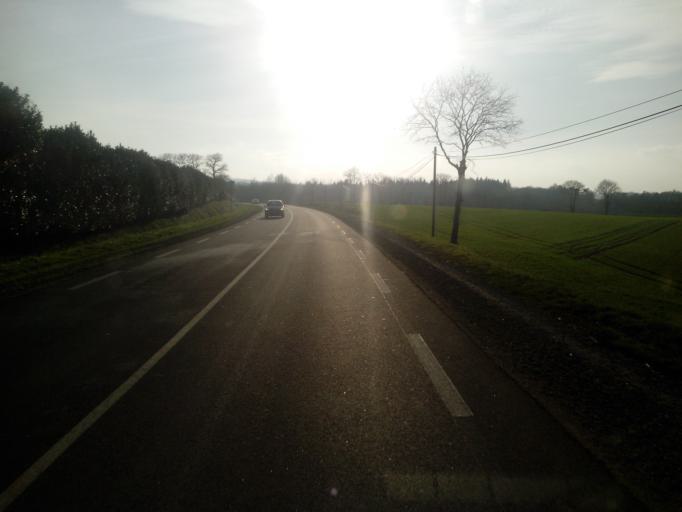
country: FR
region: Brittany
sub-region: Departement du Morbihan
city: Mauron
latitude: 48.0679
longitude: -2.2891
